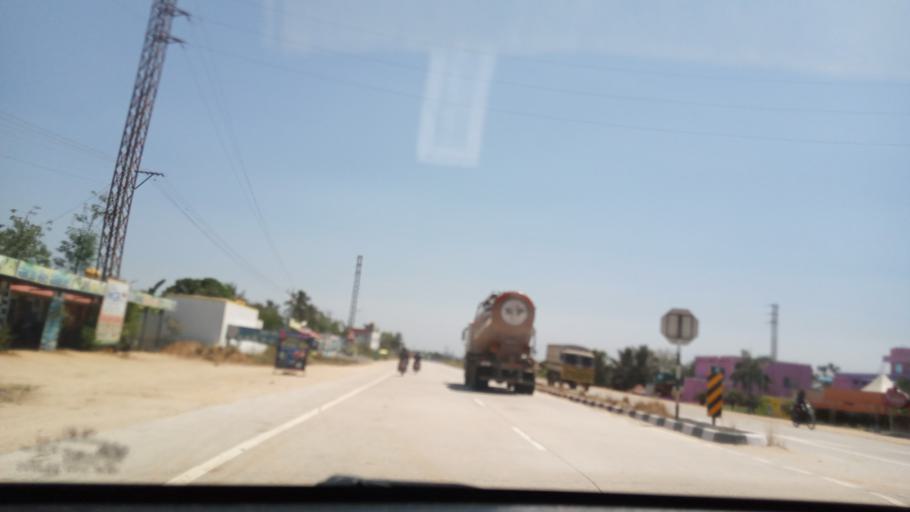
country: IN
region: Andhra Pradesh
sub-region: Chittoor
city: Chittoor
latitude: 13.1958
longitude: 79.0051
